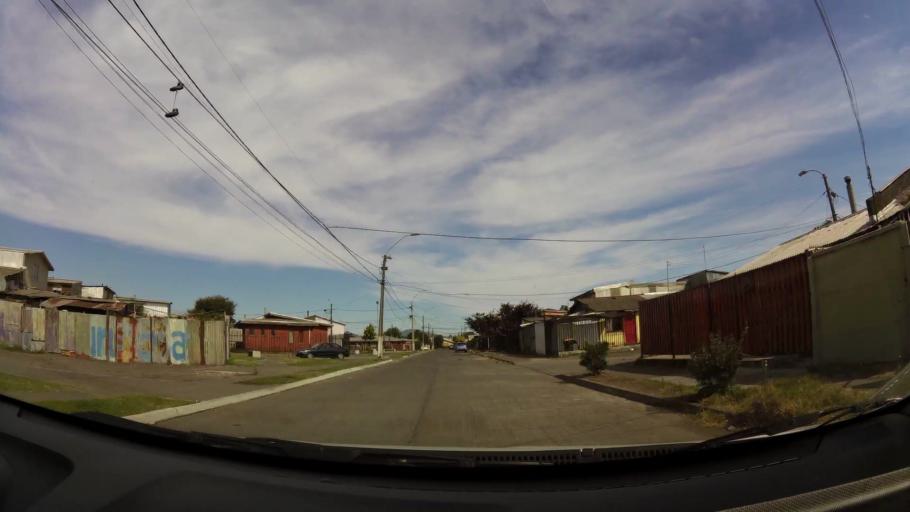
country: CL
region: Biobio
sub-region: Provincia de Concepcion
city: Talcahuano
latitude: -36.7782
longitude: -73.1080
